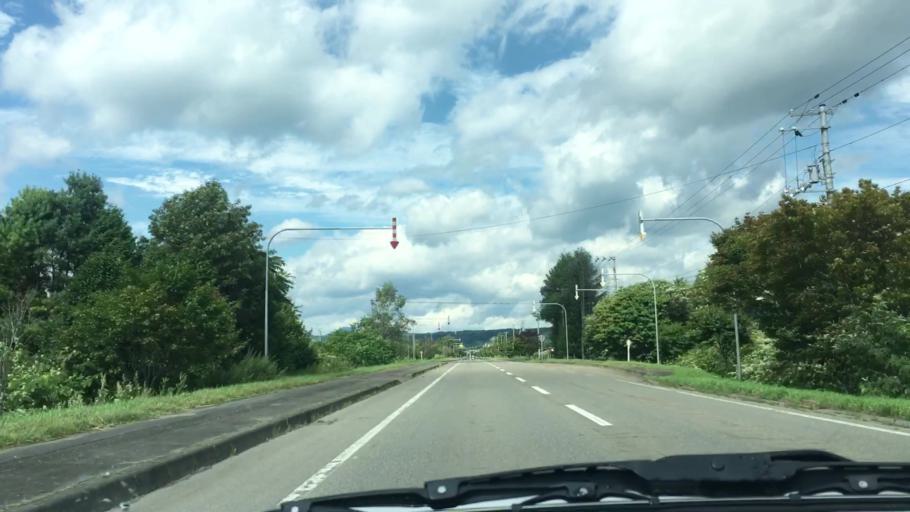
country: JP
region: Hokkaido
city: Otofuke
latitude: 43.2899
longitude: 143.3080
